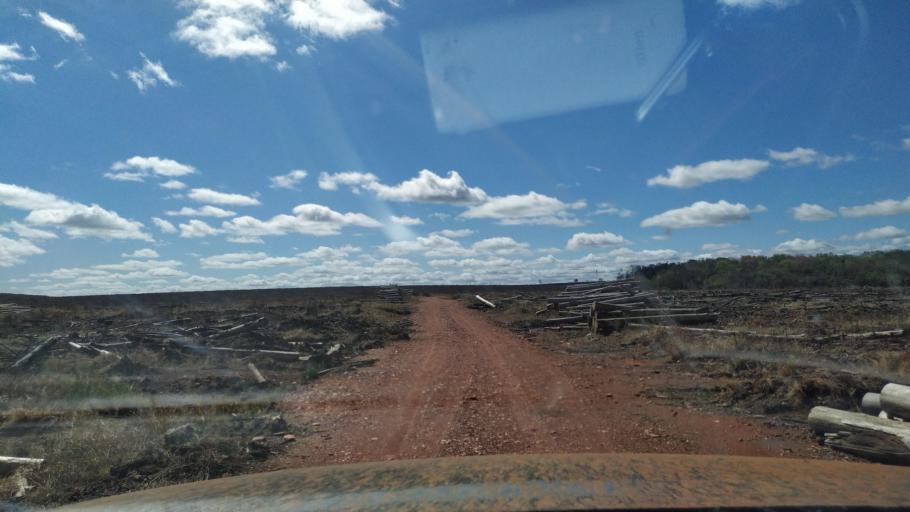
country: AR
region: Corrientes
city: Gobernador Ingeniero Valentin Virasoro
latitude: -28.2932
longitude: -56.0527
